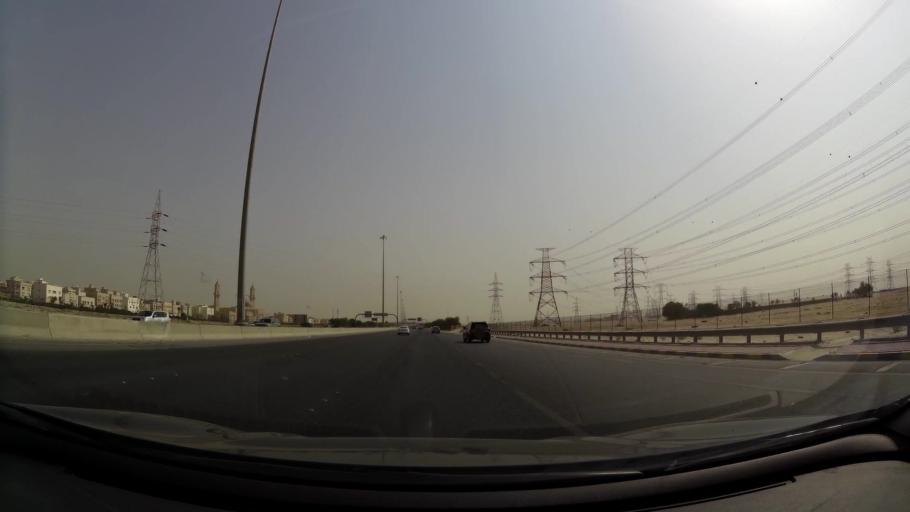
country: KW
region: Muhafazat al Jahra'
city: Al Jahra'
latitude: 29.3013
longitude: 47.6862
